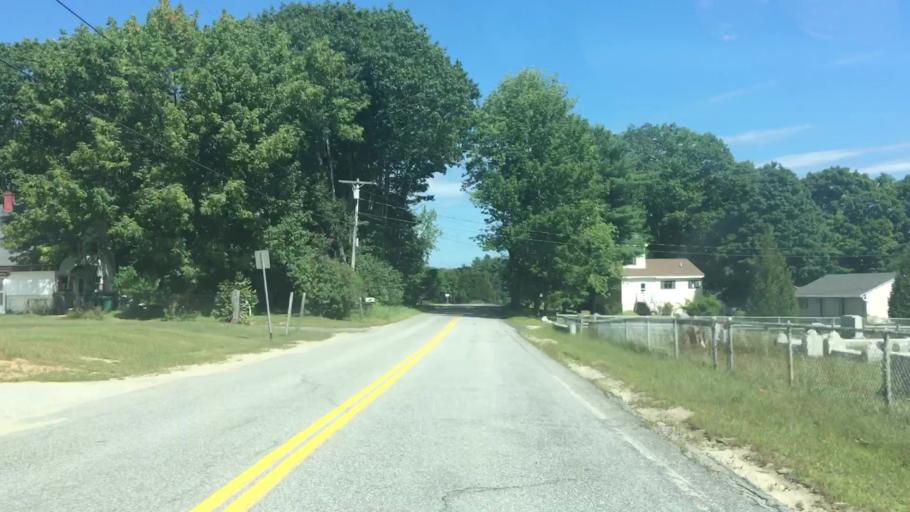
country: US
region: Maine
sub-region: Androscoggin County
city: Lisbon
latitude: 44.0633
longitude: -70.1171
